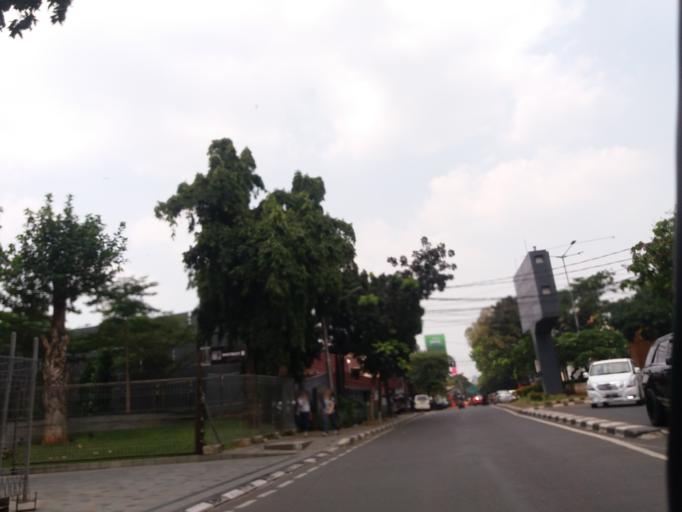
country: ID
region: Jakarta Raya
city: Jakarta
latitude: -6.2304
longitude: 106.8073
